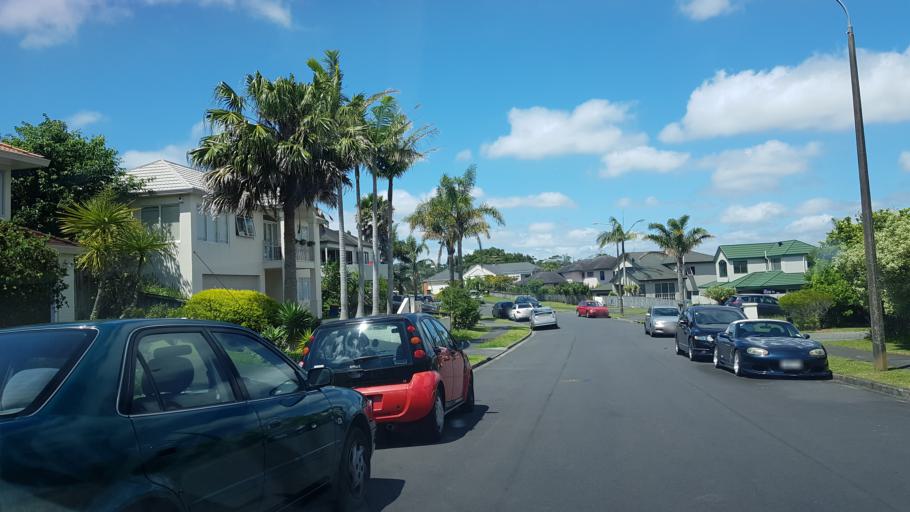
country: NZ
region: Auckland
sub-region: Auckland
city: North Shore
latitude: -36.7877
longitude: 174.7070
